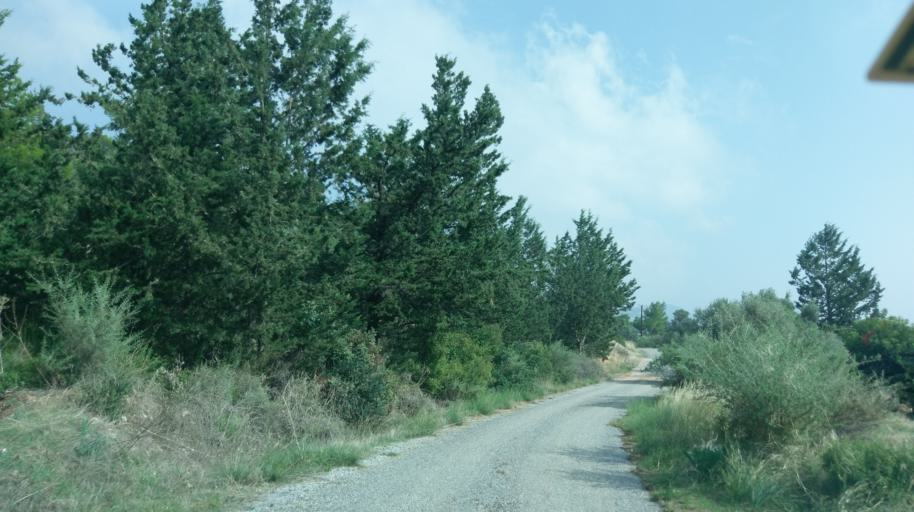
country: CY
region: Ammochostos
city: Lefkonoiko
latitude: 35.3167
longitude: 33.6206
